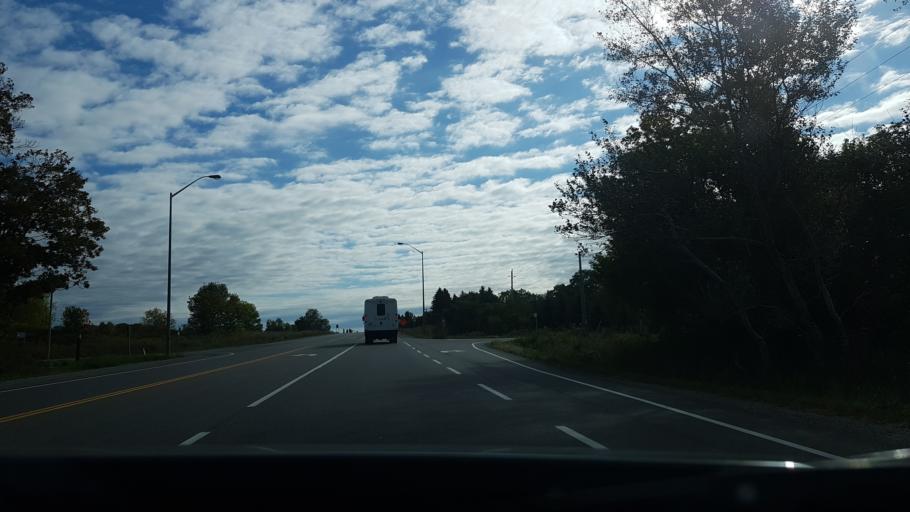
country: CA
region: Ontario
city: Orillia
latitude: 44.6129
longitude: -79.4736
